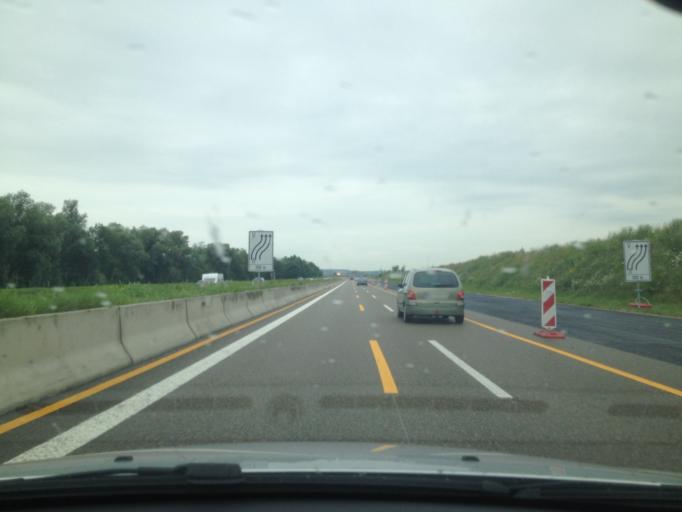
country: DE
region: Bavaria
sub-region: Swabia
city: Leipheim
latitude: 48.4587
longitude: 10.1787
